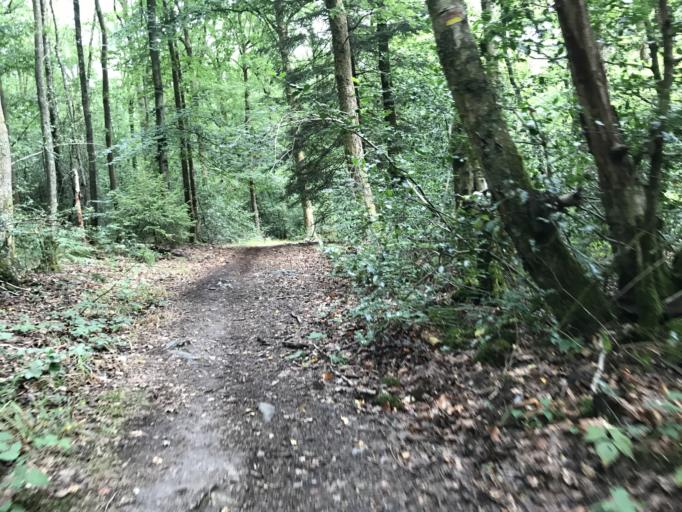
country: FR
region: Champagne-Ardenne
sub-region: Departement des Ardennes
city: Montherme
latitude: 49.8925
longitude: 4.7497
